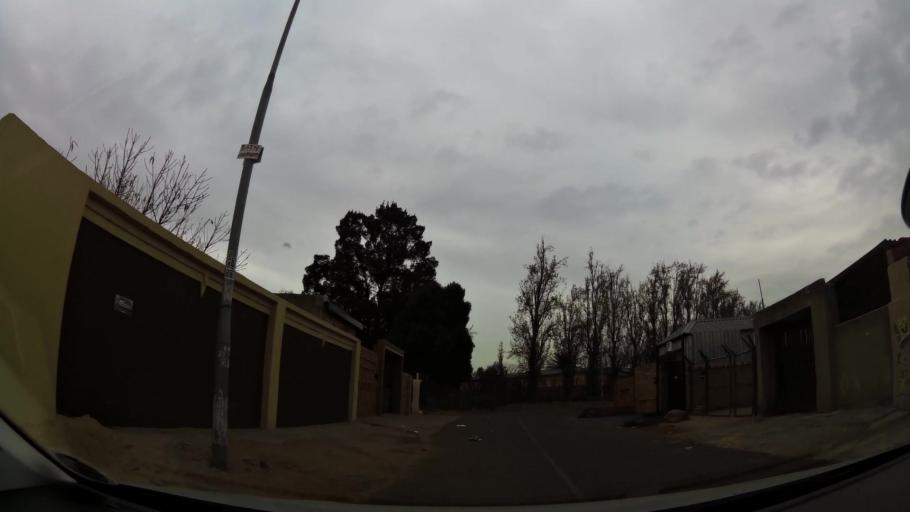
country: ZA
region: Gauteng
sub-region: City of Johannesburg Metropolitan Municipality
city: Soweto
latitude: -26.2542
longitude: 27.8732
